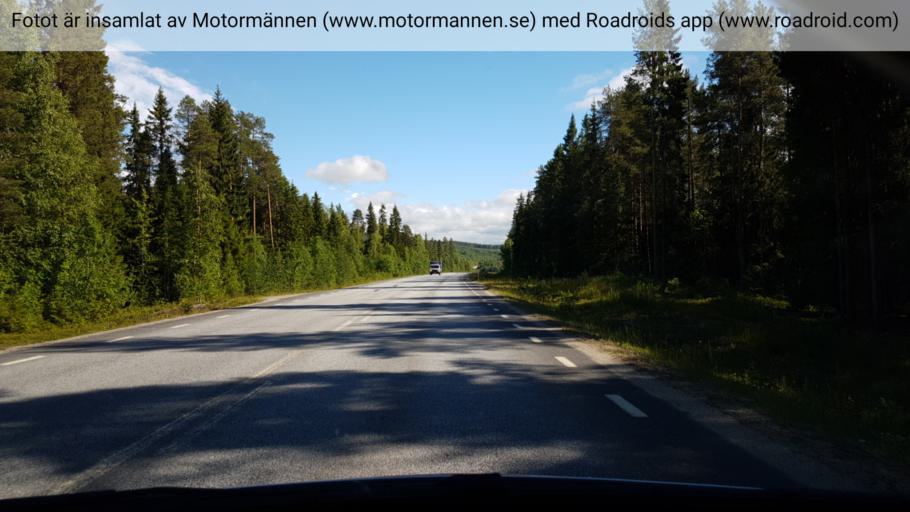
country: SE
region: Vaesterbotten
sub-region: Vannas Kommun
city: Vaennaes
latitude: 64.0039
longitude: 19.7199
